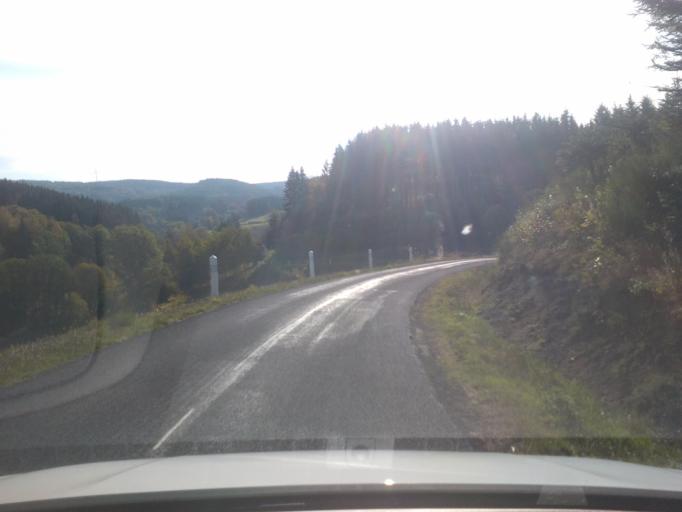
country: FR
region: Lorraine
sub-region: Departement des Vosges
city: Senones
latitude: 48.3775
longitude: 7.0475
